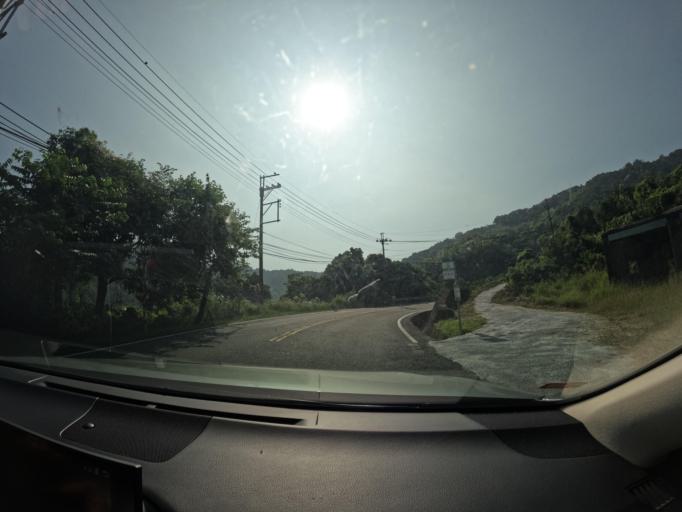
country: TW
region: Taiwan
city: Yujing
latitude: 23.0737
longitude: 120.5456
